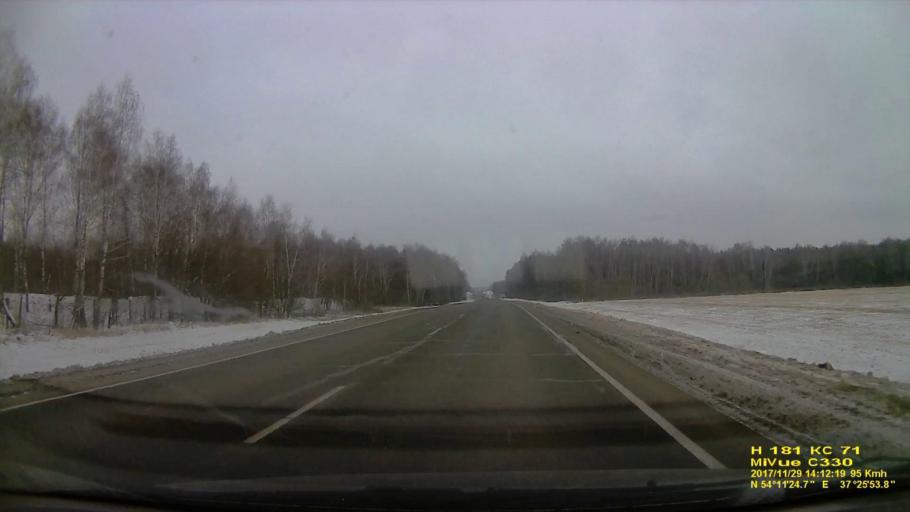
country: RU
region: Tula
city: Barsuki
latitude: 54.1900
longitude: 37.4319
